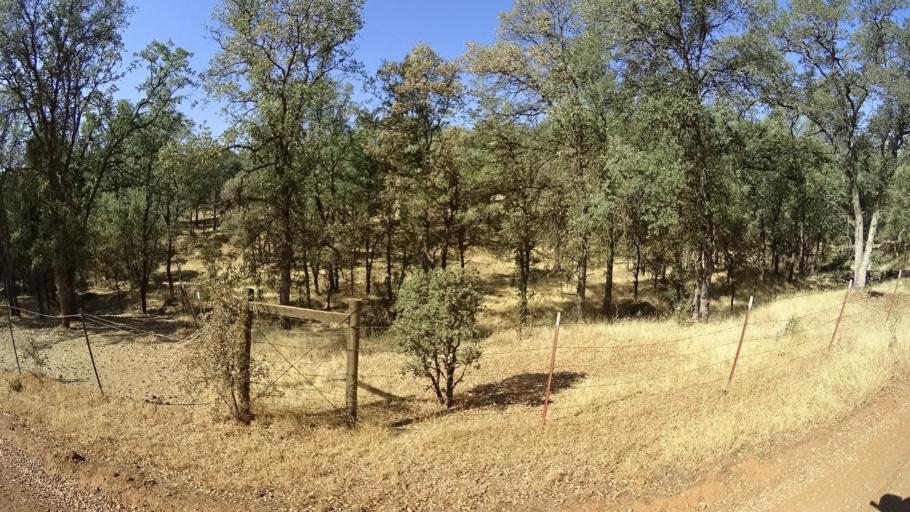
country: US
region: California
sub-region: Mariposa County
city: Mariposa
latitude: 37.6202
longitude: -120.2375
